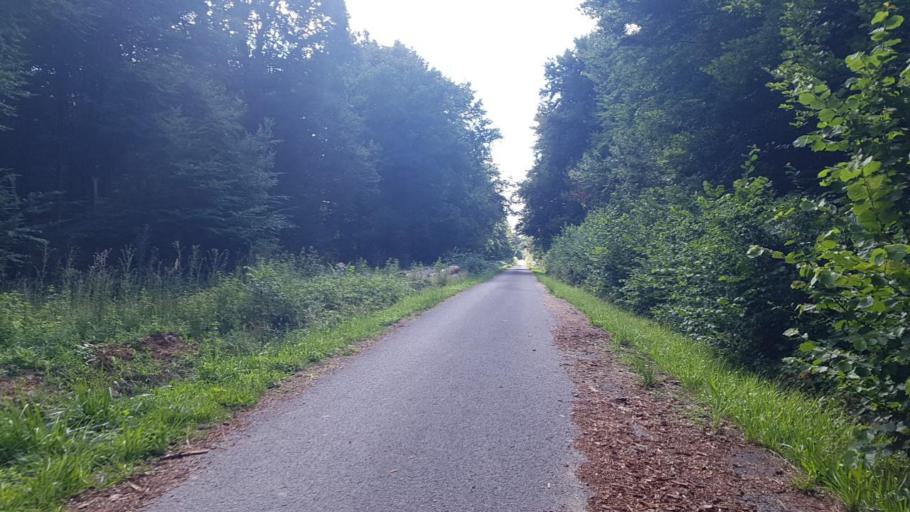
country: FR
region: Picardie
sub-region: Departement de l'Oise
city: Ver-sur-Launette
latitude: 49.1134
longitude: 2.6635
